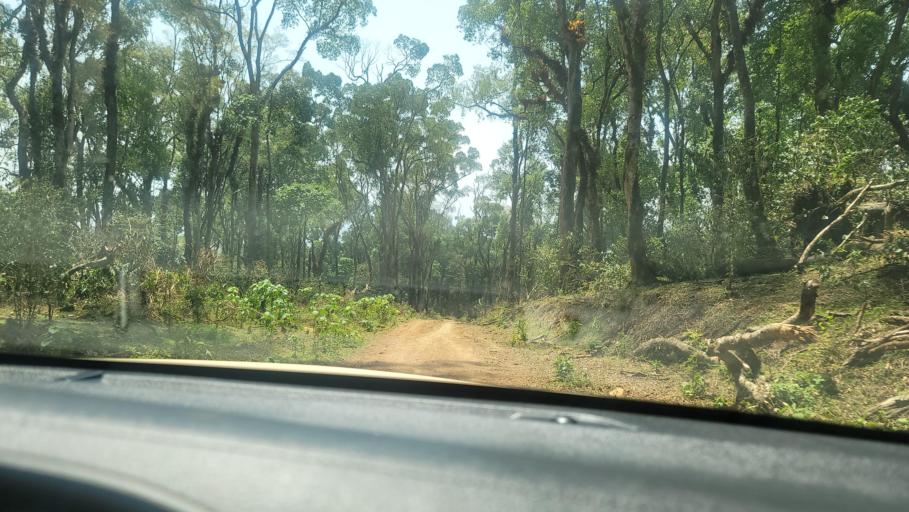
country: ET
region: Southern Nations, Nationalities, and People's Region
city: Bonga
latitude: 7.5409
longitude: 36.1809
